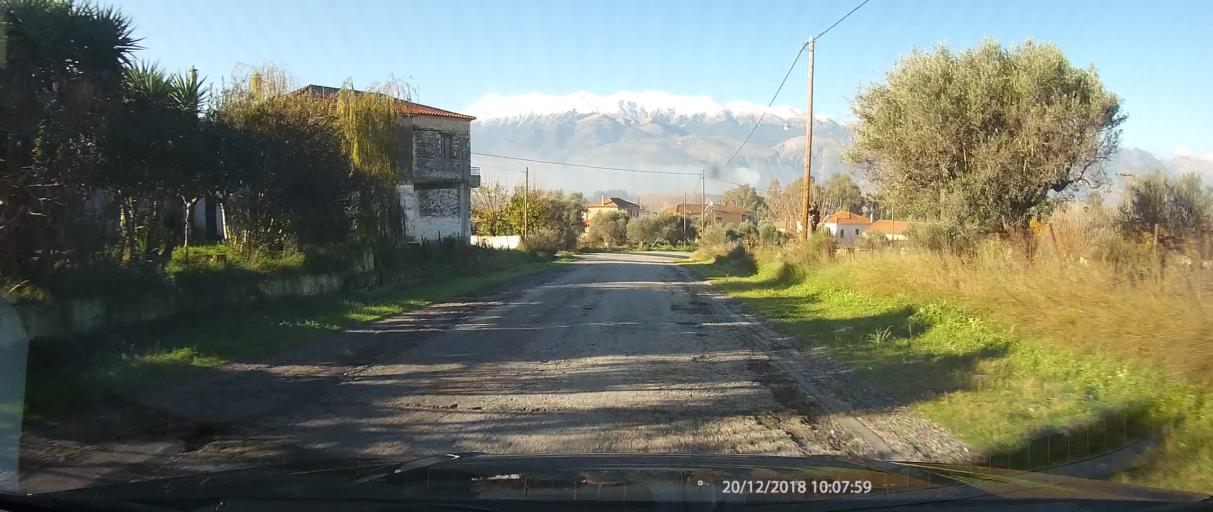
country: GR
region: Peloponnese
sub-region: Nomos Lakonias
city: Sparti
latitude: 37.0152
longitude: 22.4910
